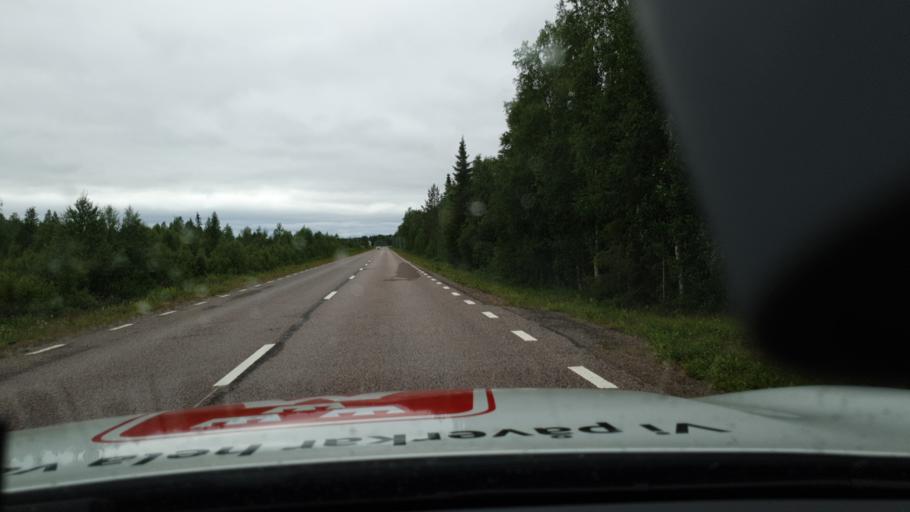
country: SE
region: Norrbotten
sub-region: Pajala Kommun
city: Pajala
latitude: 67.1988
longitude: 23.4304
